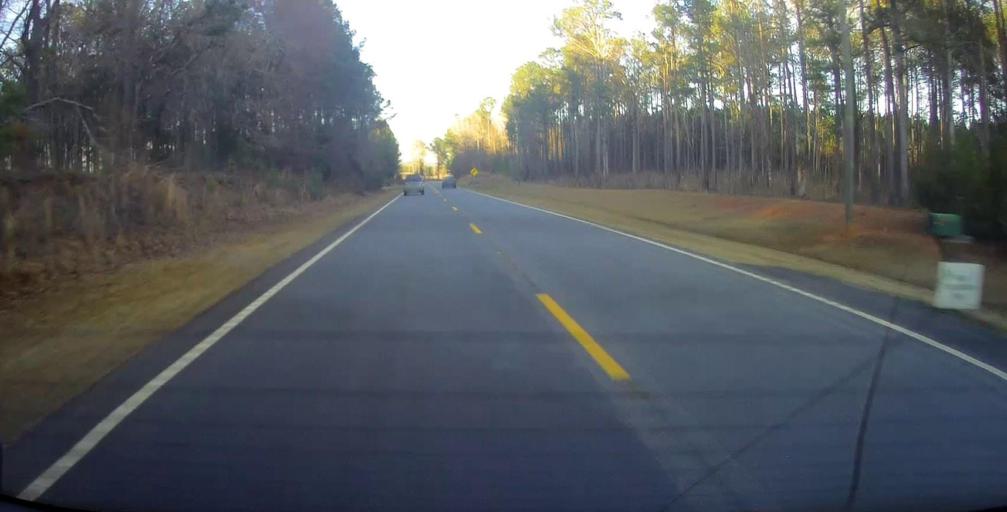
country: US
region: Georgia
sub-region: Talbot County
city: Sardis
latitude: 32.7015
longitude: -84.6996
